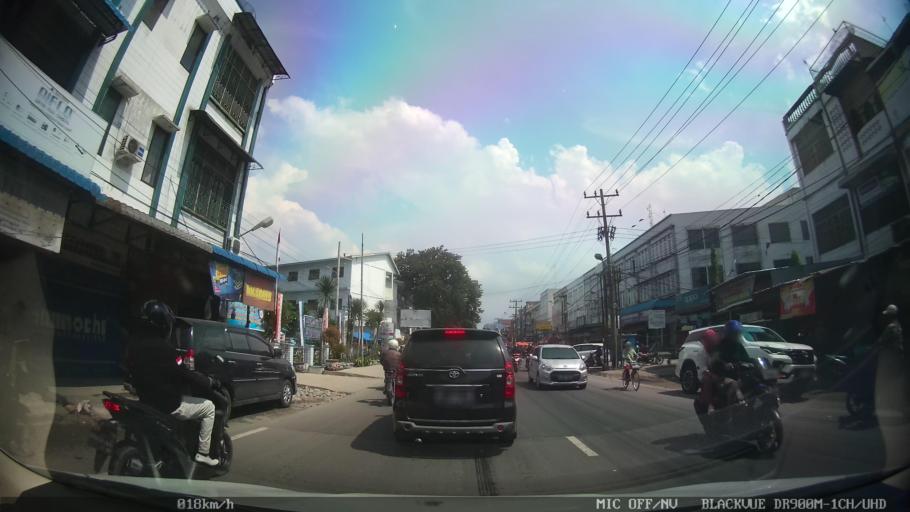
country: ID
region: North Sumatra
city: Medan
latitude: 3.6300
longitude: 98.6618
